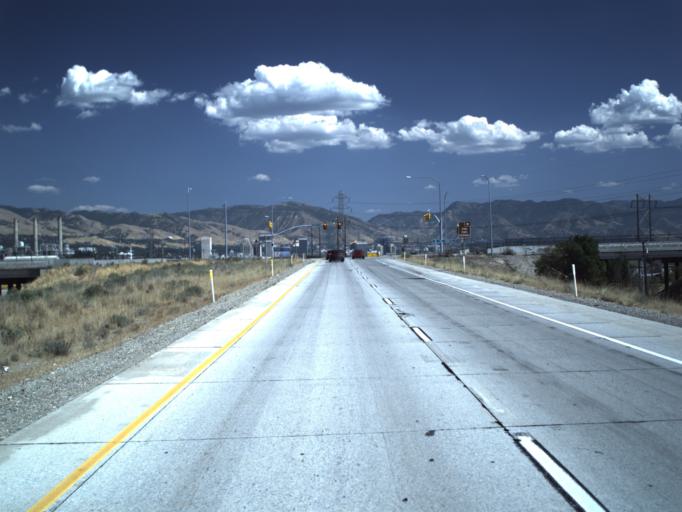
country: US
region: Utah
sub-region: Salt Lake County
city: Salt Lake City
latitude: 40.7654
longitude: -111.9411
